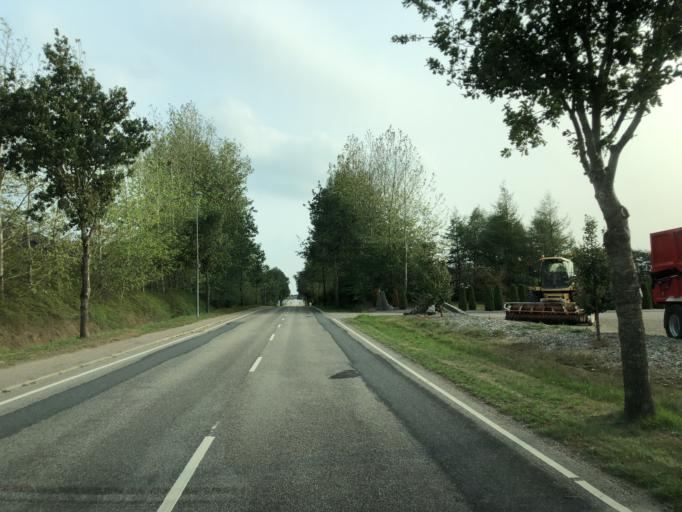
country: DK
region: Central Jutland
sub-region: Ringkobing-Skjern Kommune
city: Videbaek
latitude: 56.0944
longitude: 8.7027
